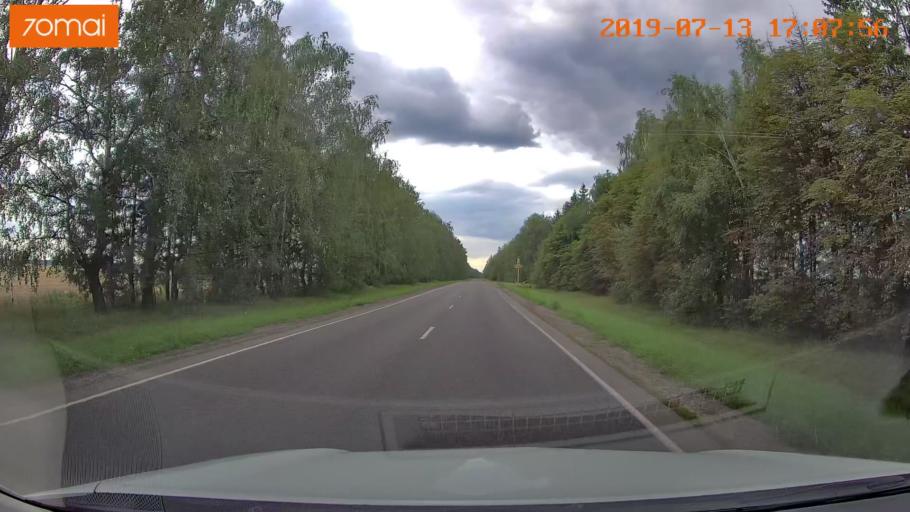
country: BY
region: Mogilev
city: Kirawsk
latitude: 53.2683
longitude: 29.3187
